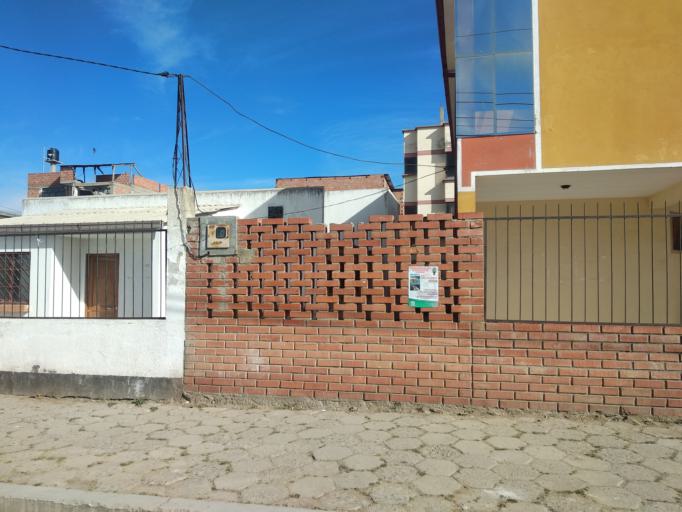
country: BO
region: La Paz
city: La Paz
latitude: -16.5309
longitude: -68.1570
